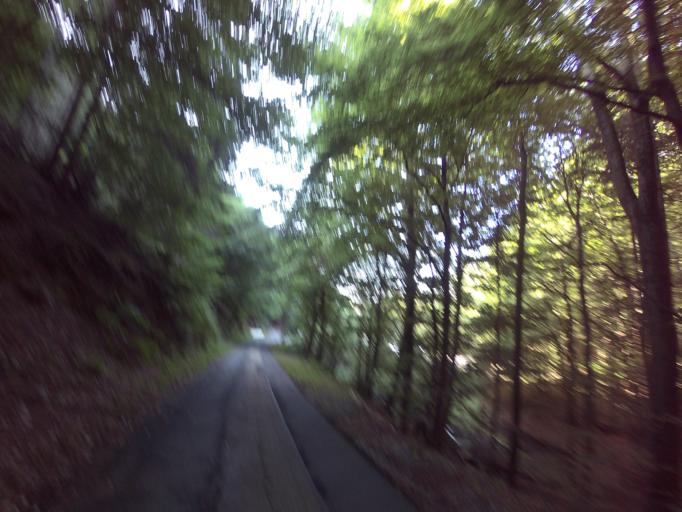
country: DE
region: North Rhine-Westphalia
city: Heimbach
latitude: 50.6104
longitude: 6.4292
